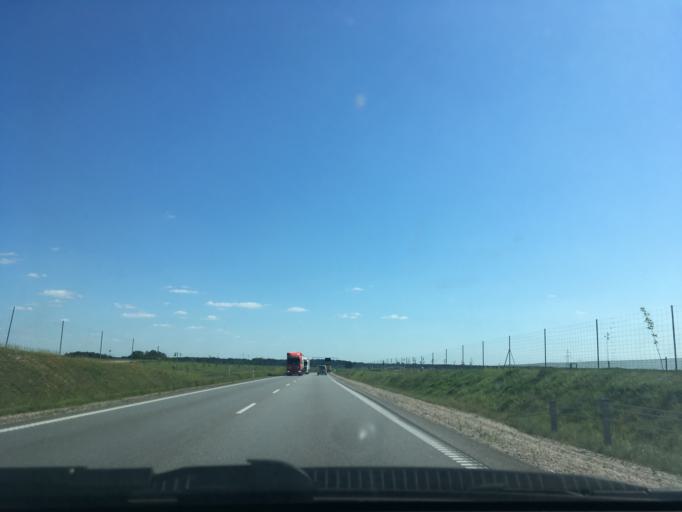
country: PL
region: Podlasie
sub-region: Powiat suwalski
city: Raczki
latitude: 53.8928
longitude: 22.8636
